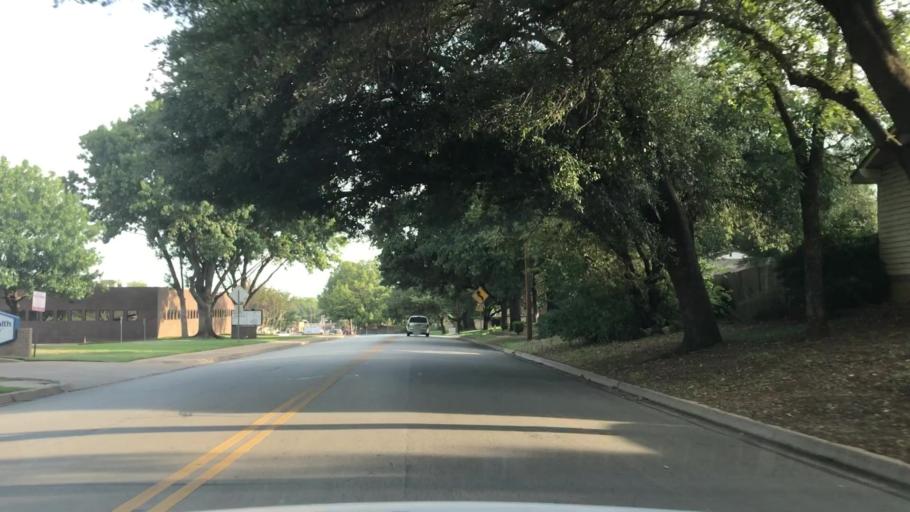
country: US
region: Texas
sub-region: Tarrant County
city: Arlington
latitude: 32.7471
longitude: -97.1229
